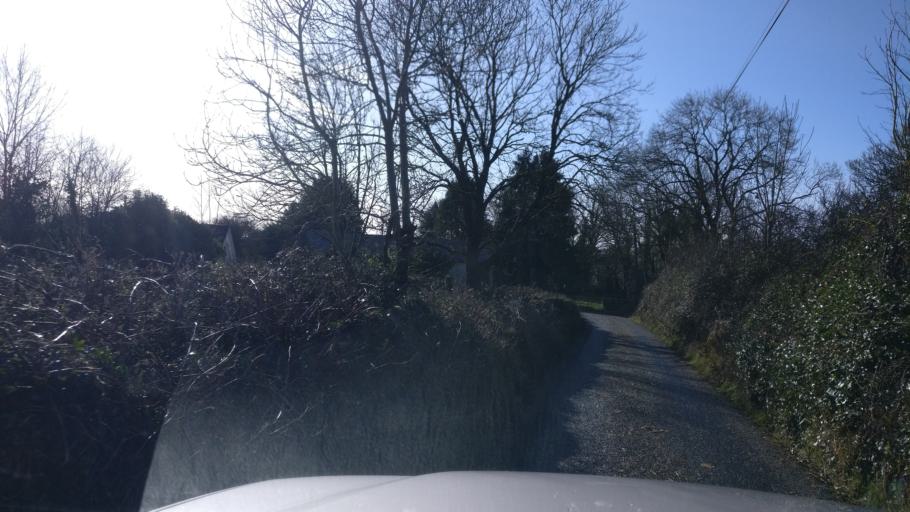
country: IE
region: Connaught
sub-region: County Galway
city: Athenry
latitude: 53.2343
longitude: -8.7794
